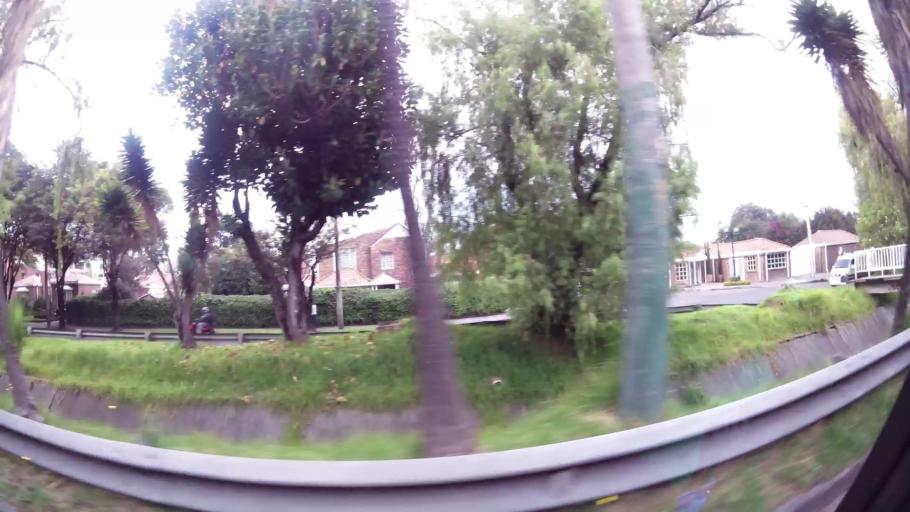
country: CO
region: Bogota D.C.
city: Barrio San Luis
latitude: 4.7151
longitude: -74.0399
